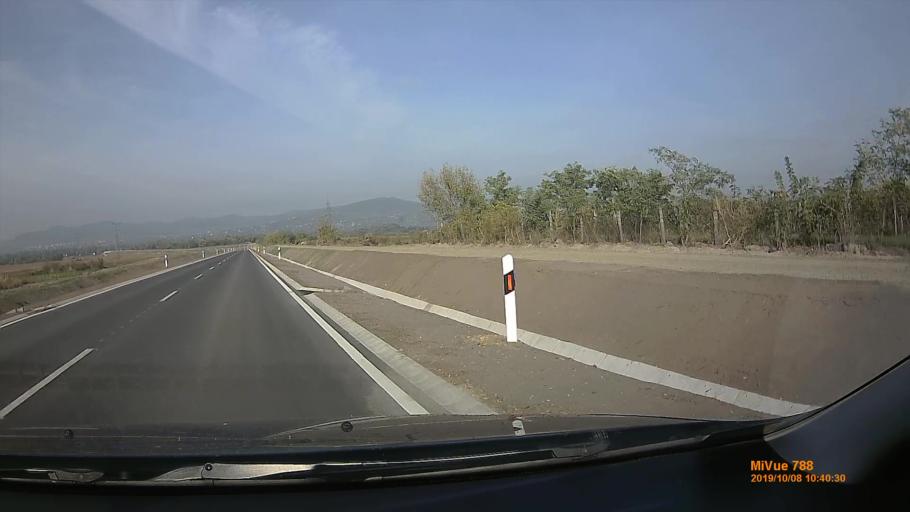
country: HU
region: Pest
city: God
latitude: 47.6620
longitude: 19.1442
